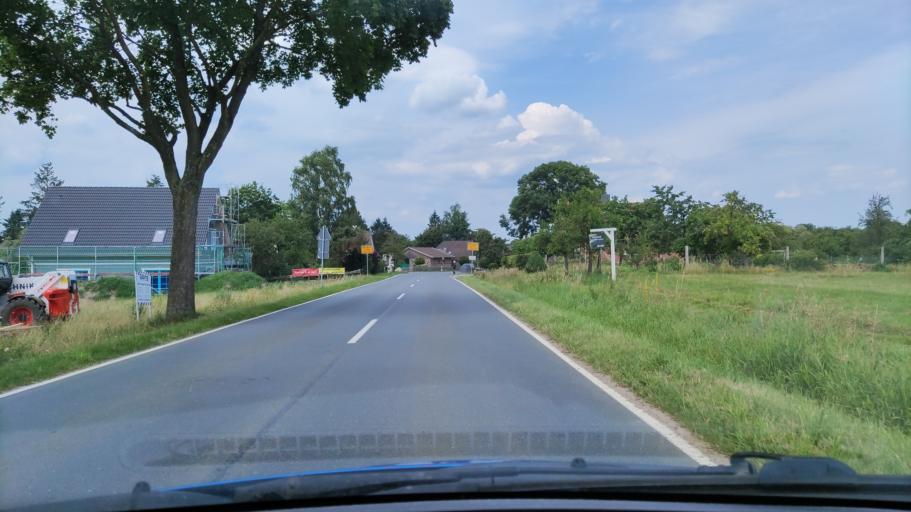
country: DE
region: Lower Saxony
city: Hanstedt
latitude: 53.2323
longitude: 10.0224
